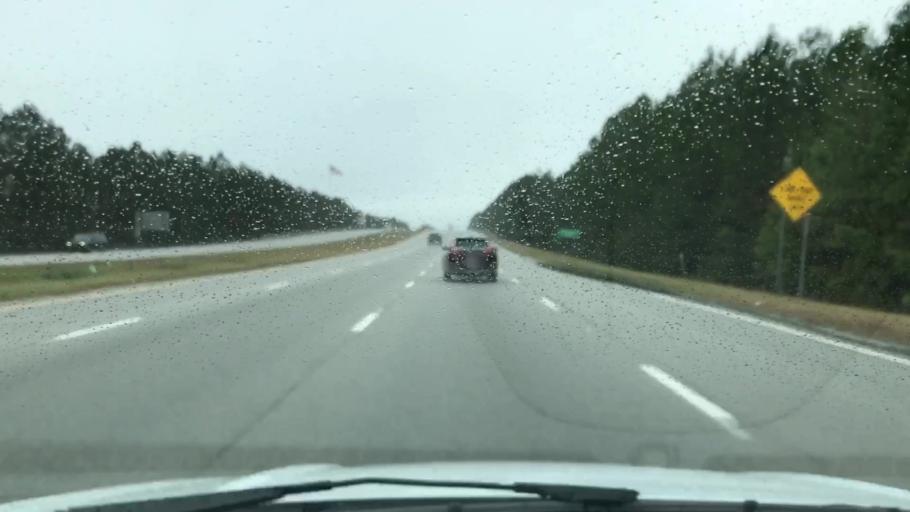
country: US
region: South Carolina
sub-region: Horry County
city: Myrtle Beach
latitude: 33.7518
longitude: -78.8637
